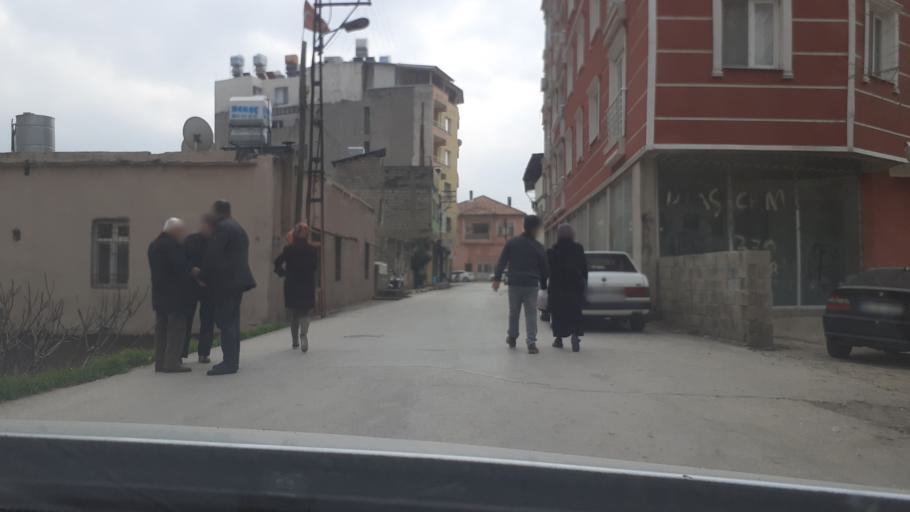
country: TR
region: Hatay
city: Kirikhan
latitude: 36.4972
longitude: 36.3538
